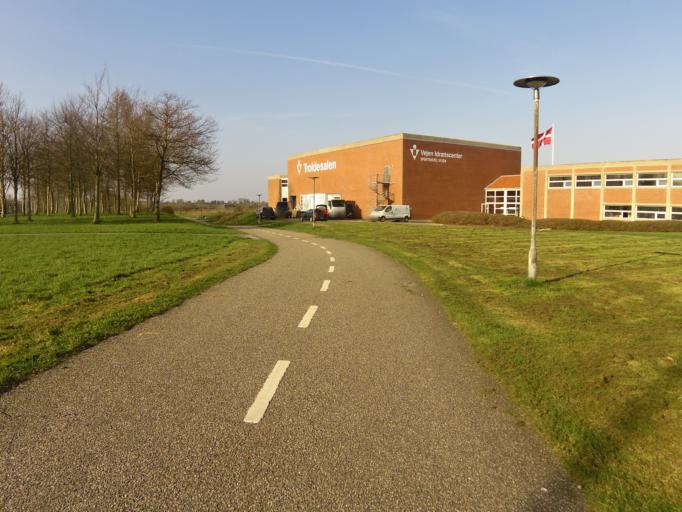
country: DK
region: South Denmark
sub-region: Vejen Kommune
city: Vejen
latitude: 55.4724
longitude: 9.1233
